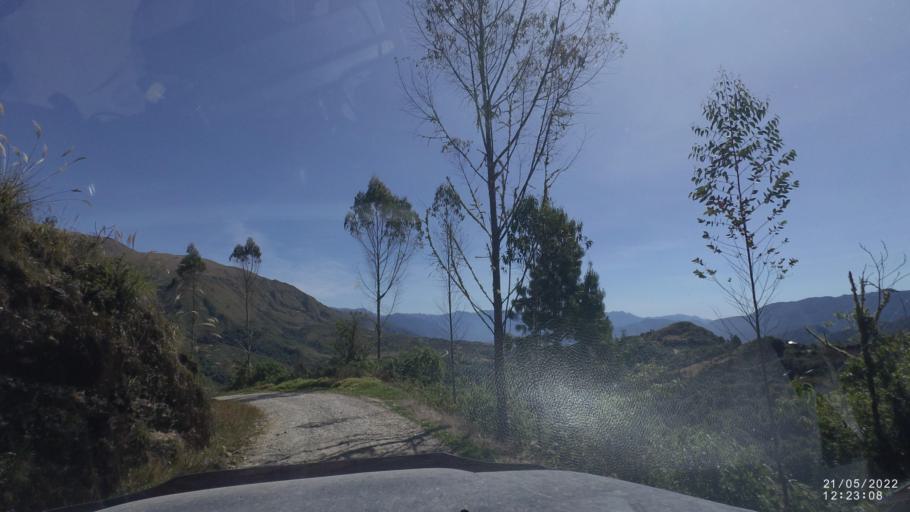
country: BO
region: Cochabamba
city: Colomi
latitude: -17.2216
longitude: -65.9042
